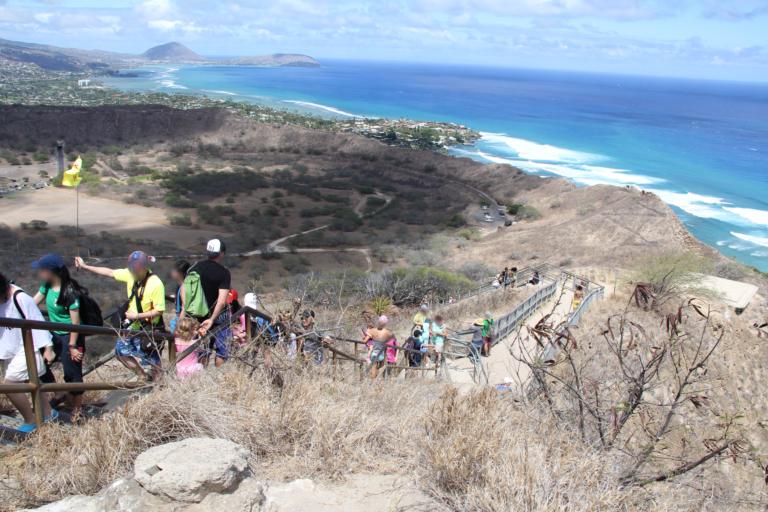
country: US
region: Hawaii
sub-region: Honolulu County
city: Honolulu
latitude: 21.2597
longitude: -157.8117
